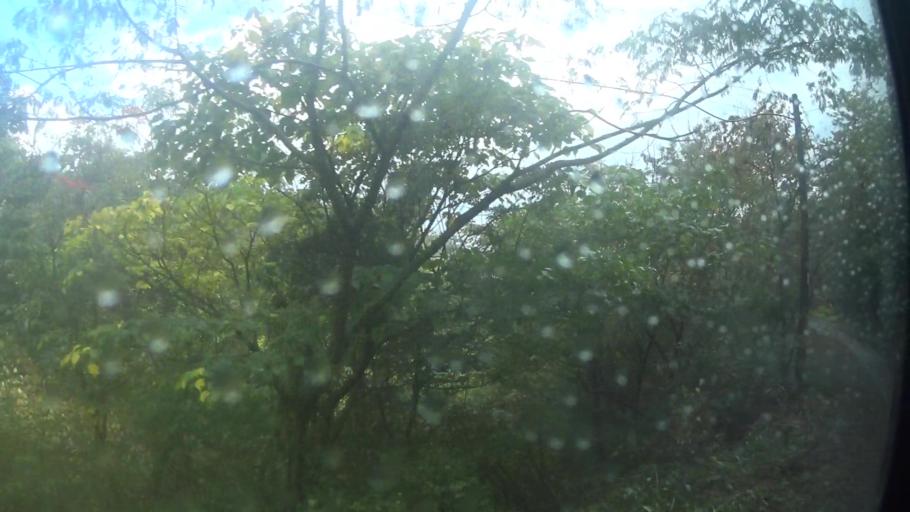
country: JP
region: Kyoto
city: Miyazu
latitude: 35.5859
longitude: 135.1925
